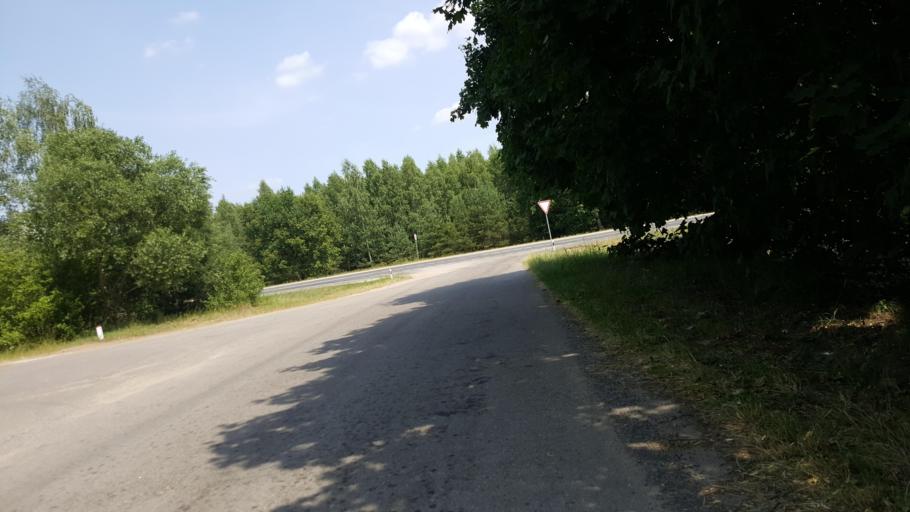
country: BY
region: Brest
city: Kamyanyets
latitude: 52.3438
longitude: 23.7793
